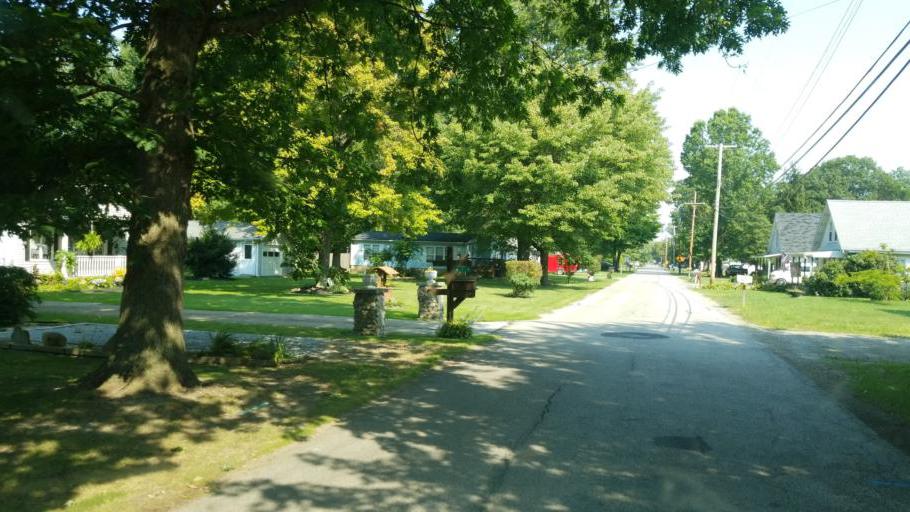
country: US
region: Ohio
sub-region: Lake County
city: Painesville
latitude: 41.7622
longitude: -81.2248
